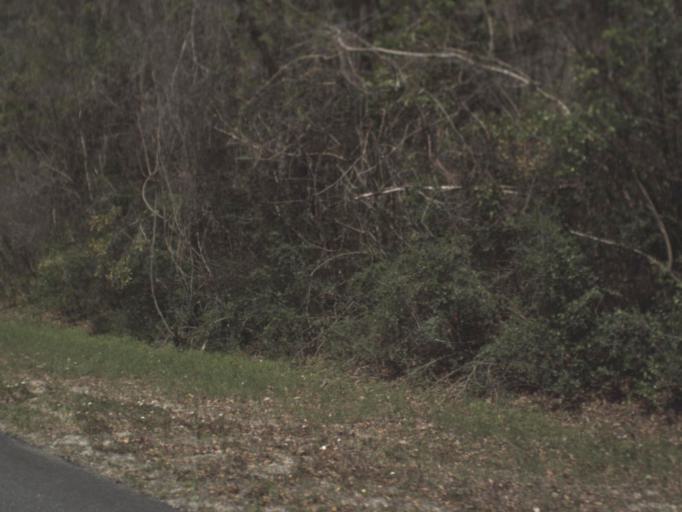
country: US
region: Florida
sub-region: Leon County
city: Woodville
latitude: 30.2386
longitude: -84.2676
